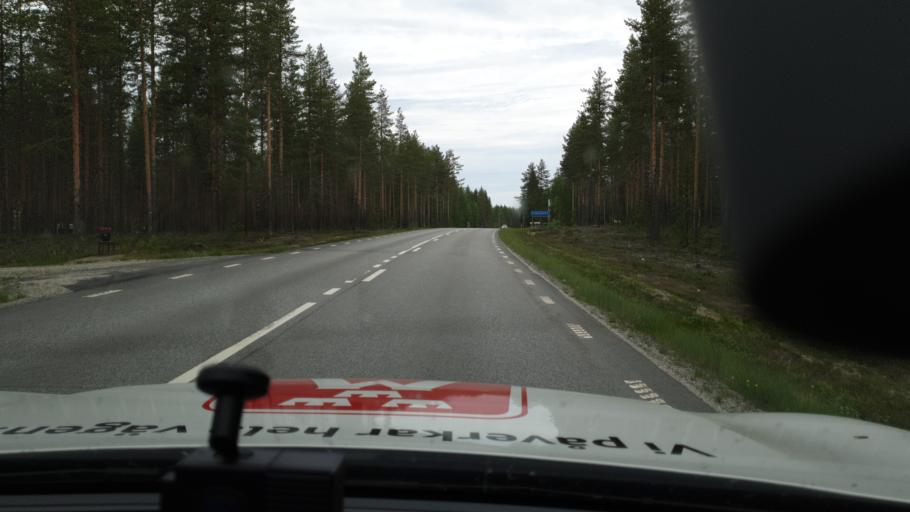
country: SE
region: Vaesterbotten
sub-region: Lycksele Kommun
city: Lycksele
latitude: 64.5284
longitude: 18.7735
